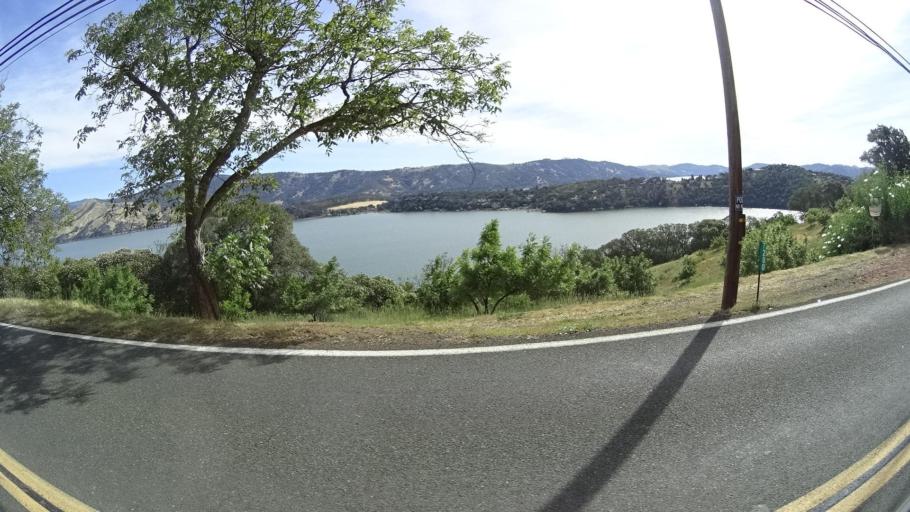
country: US
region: California
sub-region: Lake County
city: Soda Bay
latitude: 39.0085
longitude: -122.7727
